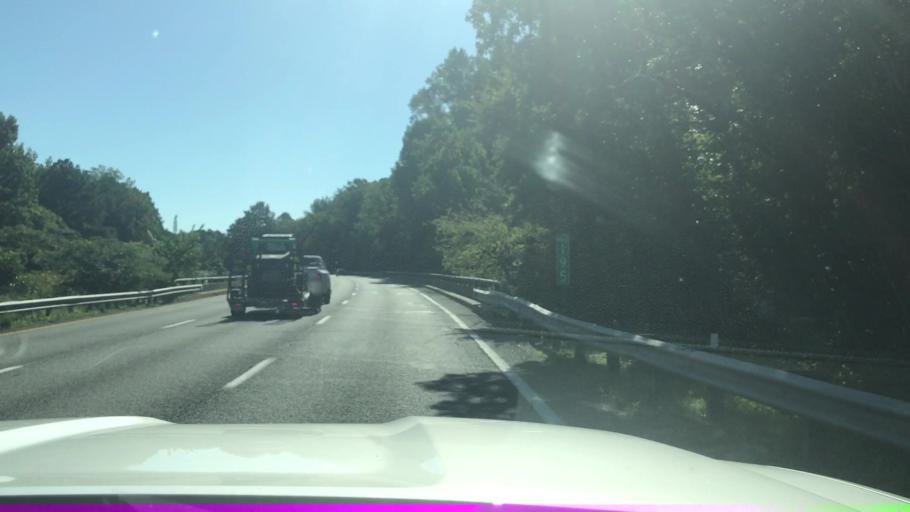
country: US
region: Virginia
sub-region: Henrico County
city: Montrose
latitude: 37.5300
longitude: -77.3743
